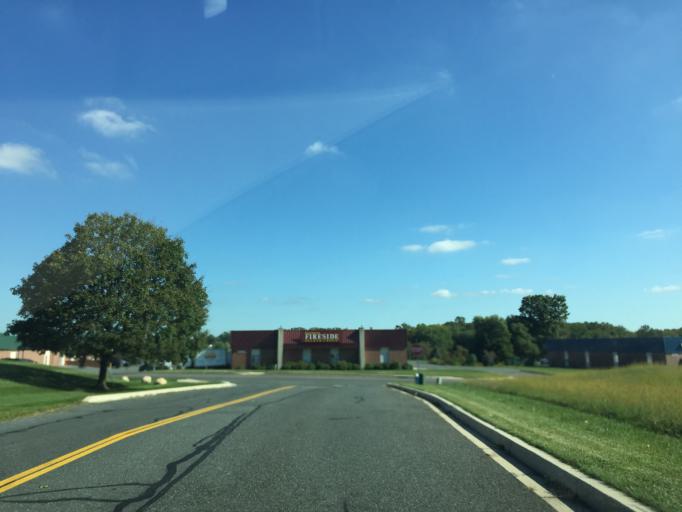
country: US
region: Maryland
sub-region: Harford County
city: Bel Air North
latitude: 39.5764
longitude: -76.3700
